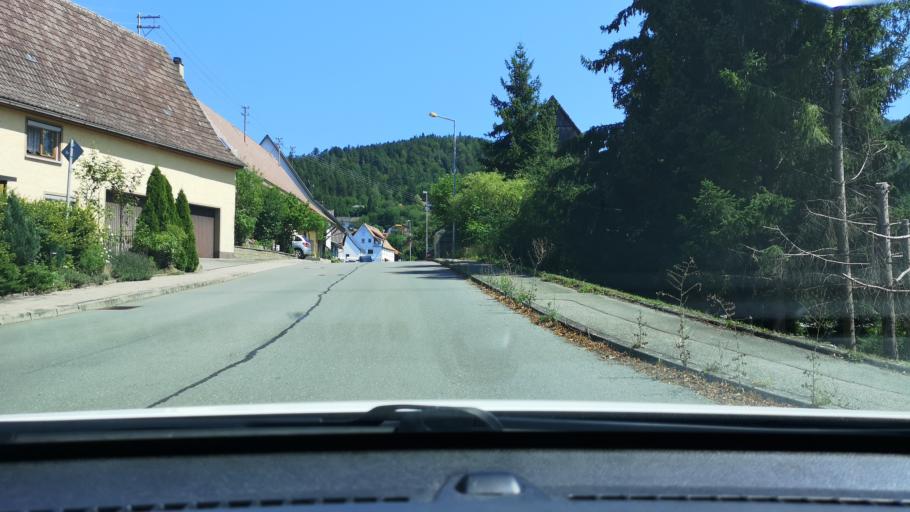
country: DE
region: Baden-Wuerttemberg
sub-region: Freiburg Region
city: Muhlheim am Bach
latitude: 48.3689
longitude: 8.7049
